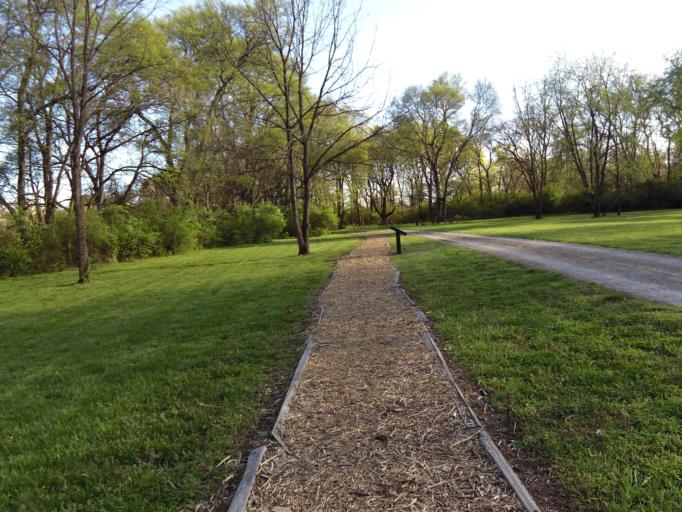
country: US
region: Tennessee
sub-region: Davidson County
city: Lakewood
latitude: 36.2187
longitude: -86.6114
